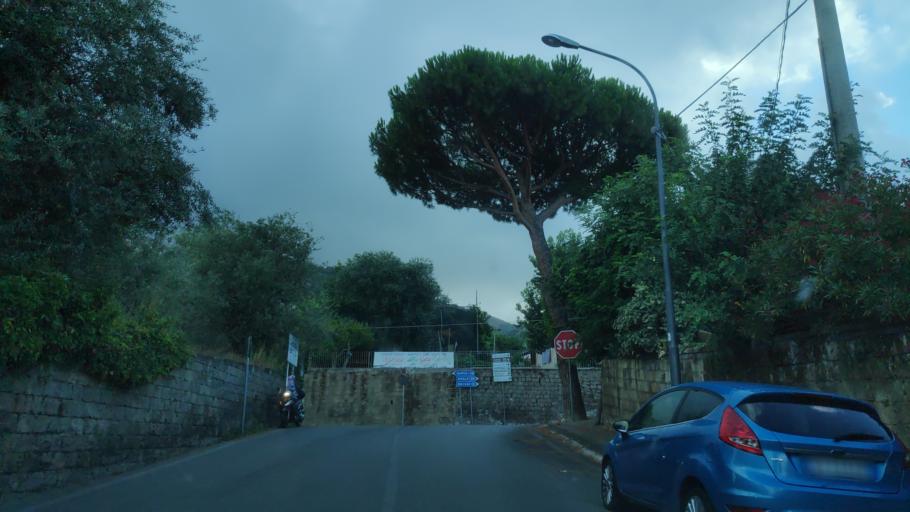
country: IT
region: Campania
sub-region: Provincia di Napoli
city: Piano di Sorrento
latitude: 40.6290
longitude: 14.4234
